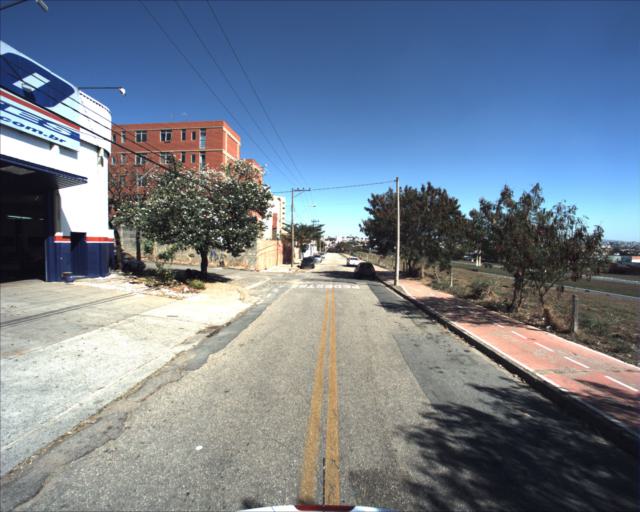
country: BR
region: Sao Paulo
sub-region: Sorocaba
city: Sorocaba
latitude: -23.4764
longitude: -47.4352
